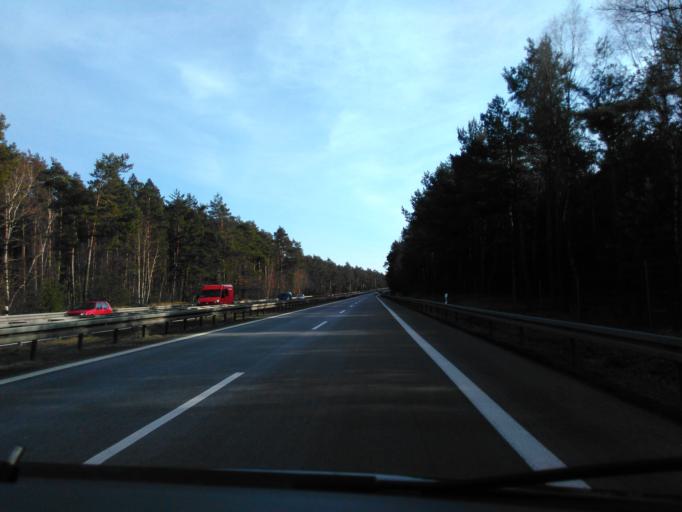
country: DE
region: Brandenburg
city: Bronkow
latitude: 51.7167
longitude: 13.8892
